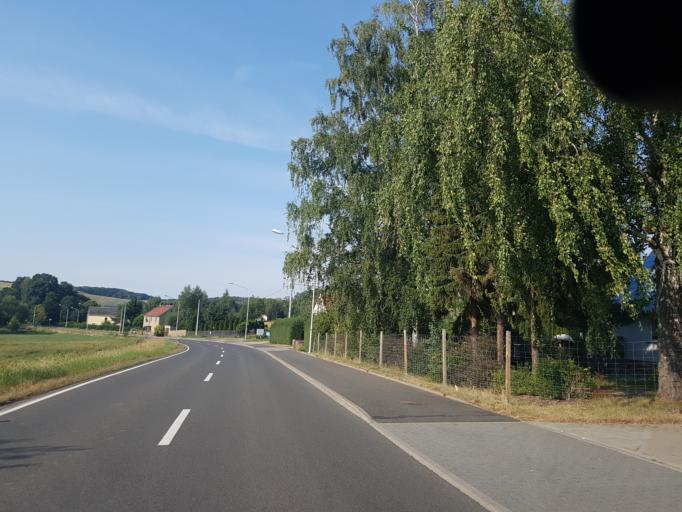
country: DE
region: Saxony
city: Waldheim
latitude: 51.0858
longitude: 13.0656
